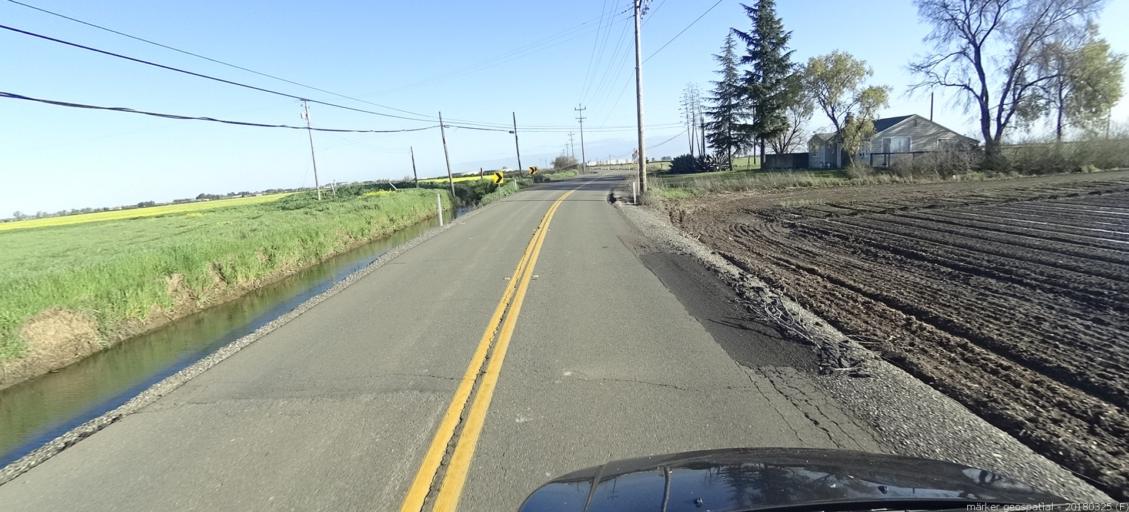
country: US
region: California
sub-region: Yolo County
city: West Sacramento
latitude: 38.6626
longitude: -121.5766
